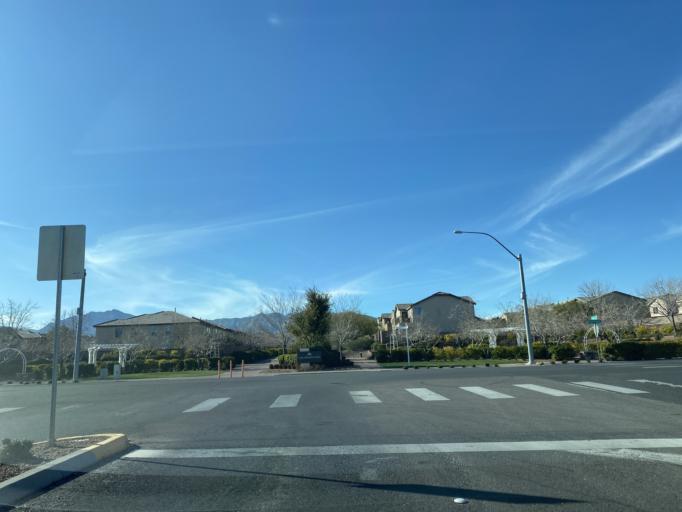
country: US
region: Nevada
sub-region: Clark County
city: Summerlin South
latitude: 36.2920
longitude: -115.3192
